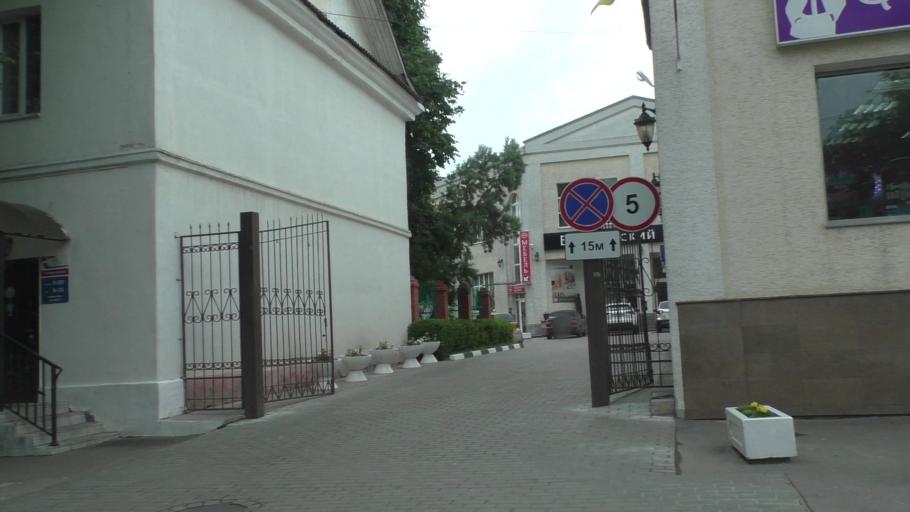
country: RU
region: Moskovskaya
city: Yegor'yevsk
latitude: 55.3806
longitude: 39.0400
